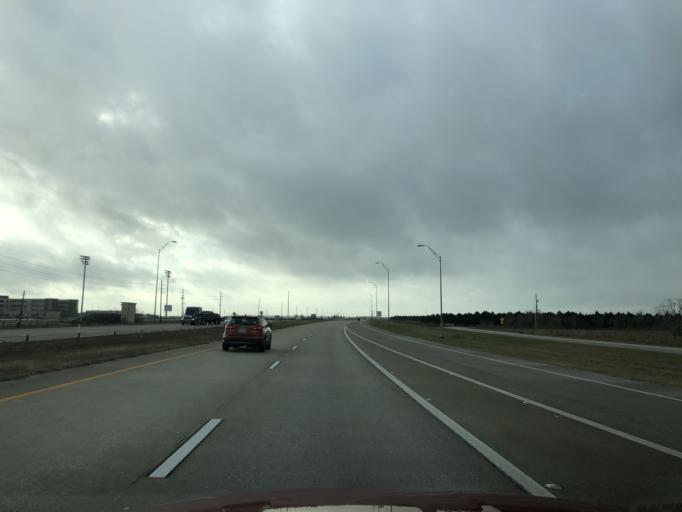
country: US
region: Texas
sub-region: Harris County
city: Cypress
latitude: 29.9355
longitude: -95.7640
